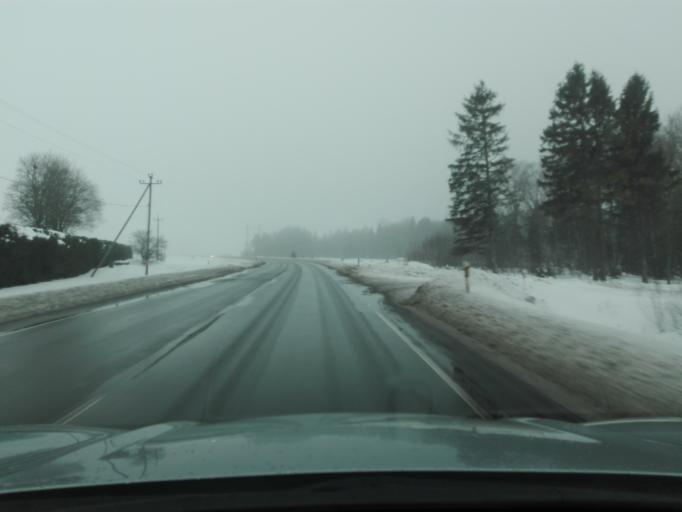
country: EE
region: Raplamaa
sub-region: Kohila vald
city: Kohila
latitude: 59.2173
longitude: 24.7762
